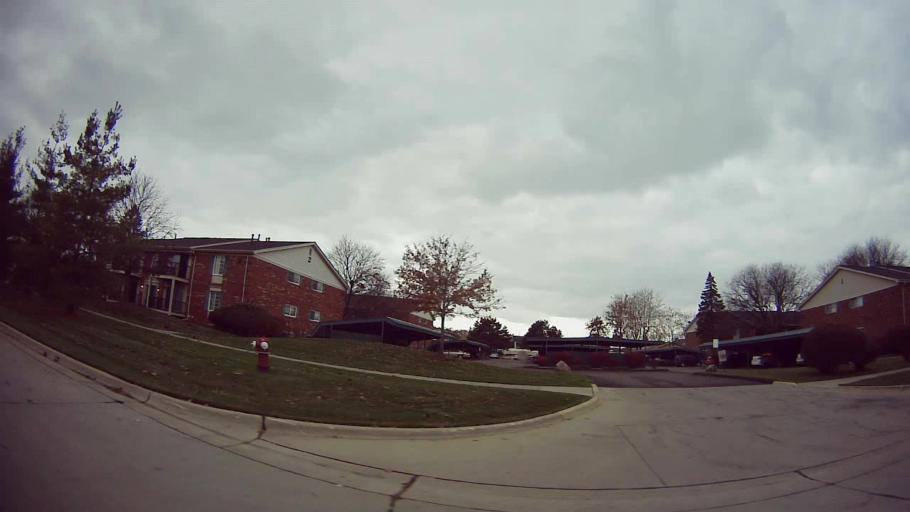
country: US
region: Michigan
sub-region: Macomb County
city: Sterling Heights
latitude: 42.5508
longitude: -83.0045
